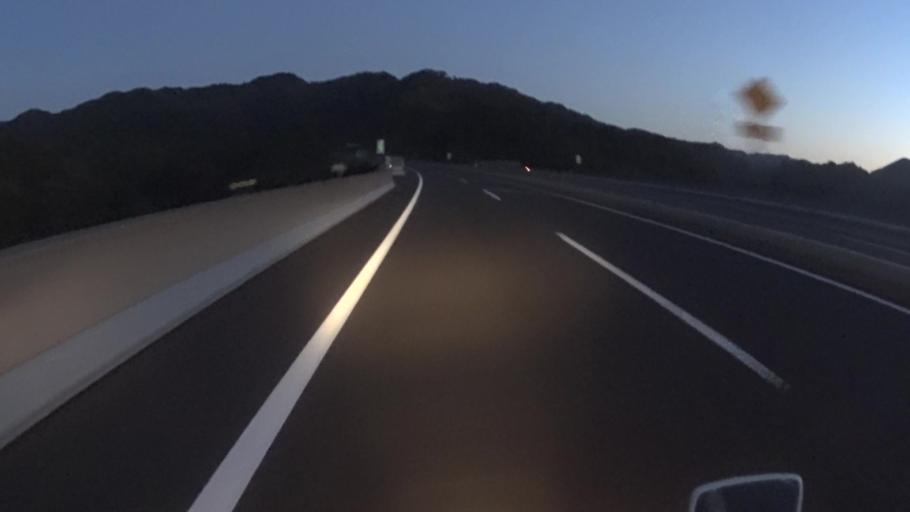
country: JP
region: Kyoto
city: Miyazu
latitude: 35.4215
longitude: 135.2126
